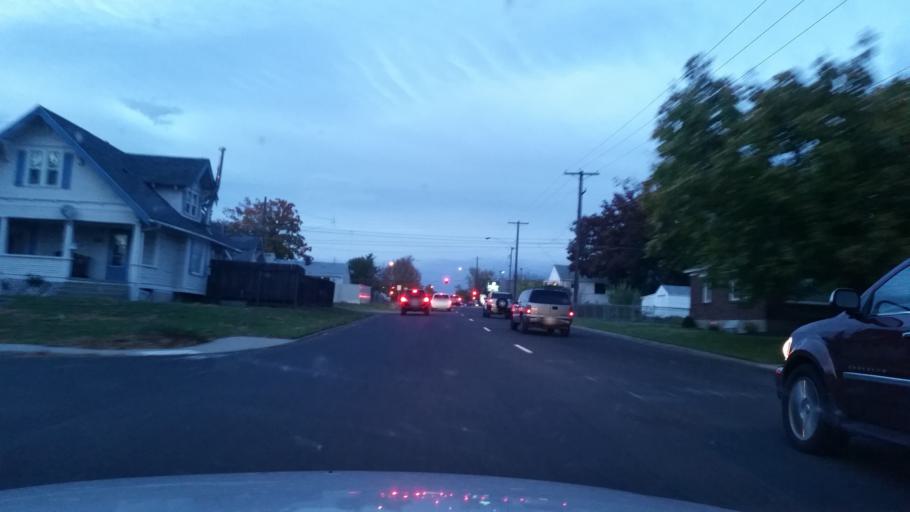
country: US
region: Washington
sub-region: Spokane County
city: Spokane
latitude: 47.6920
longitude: -117.4351
